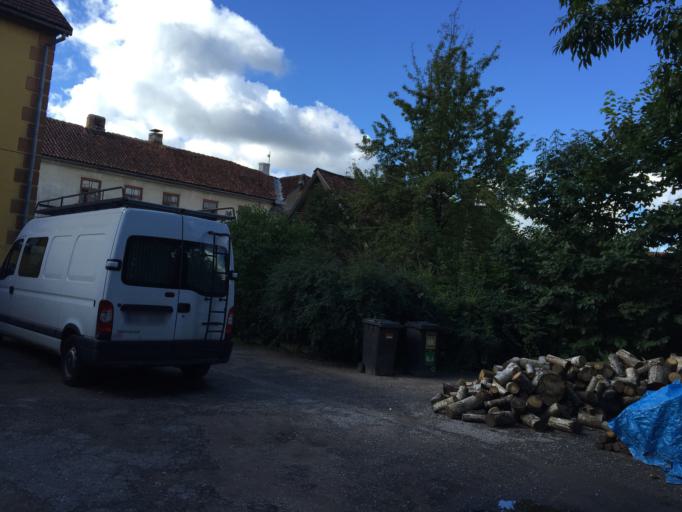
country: LV
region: Kuldigas Rajons
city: Kuldiga
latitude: 56.9678
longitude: 21.9724
